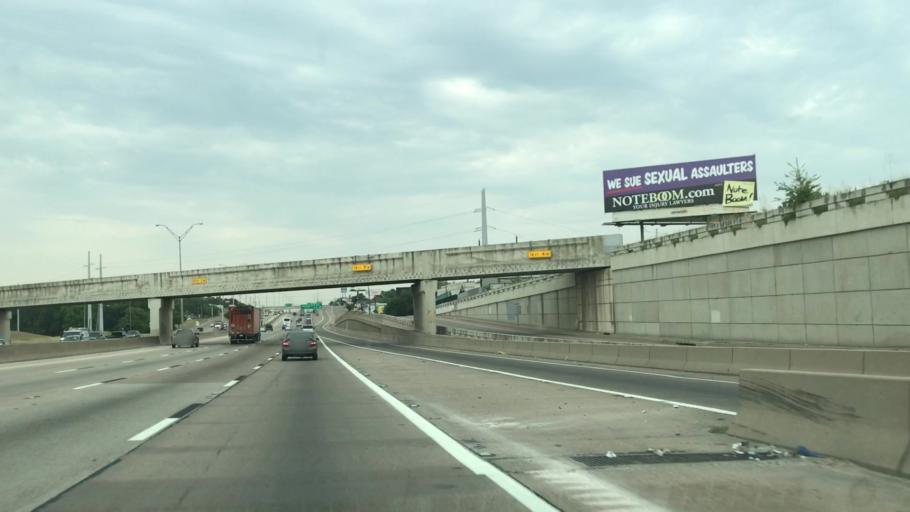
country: US
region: Texas
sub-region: Tarrant County
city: Fort Worth
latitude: 32.7044
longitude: -97.3208
